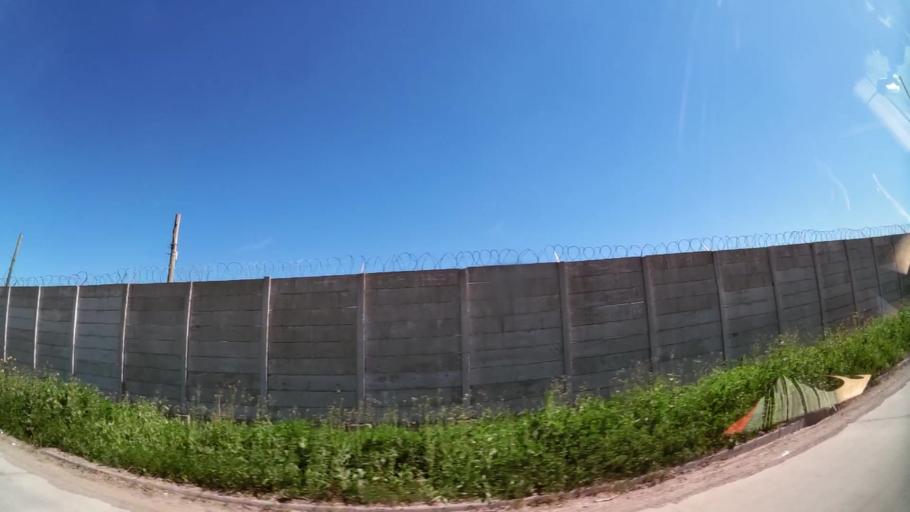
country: AR
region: Buenos Aires
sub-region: Partido de Tigre
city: Tigre
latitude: -34.4982
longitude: -58.6057
